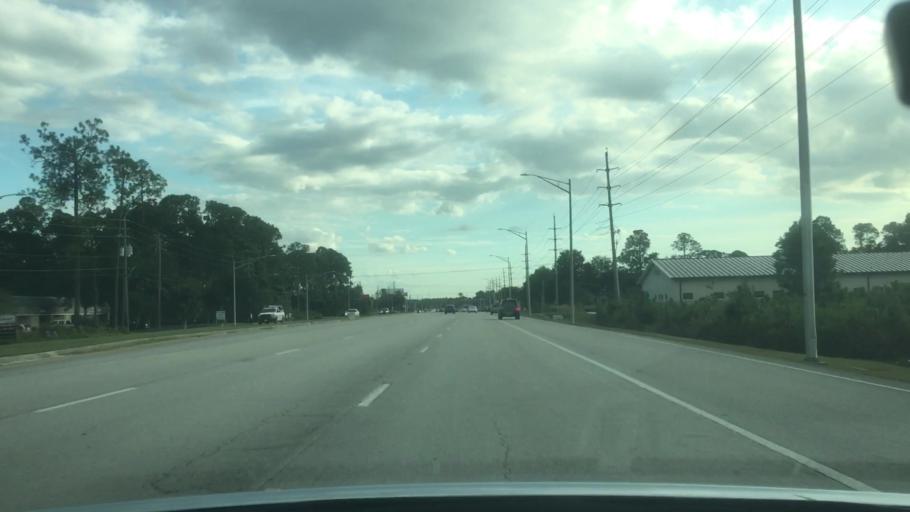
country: US
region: Florida
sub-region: Duval County
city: Neptune Beach
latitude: 30.2912
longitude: -81.5259
